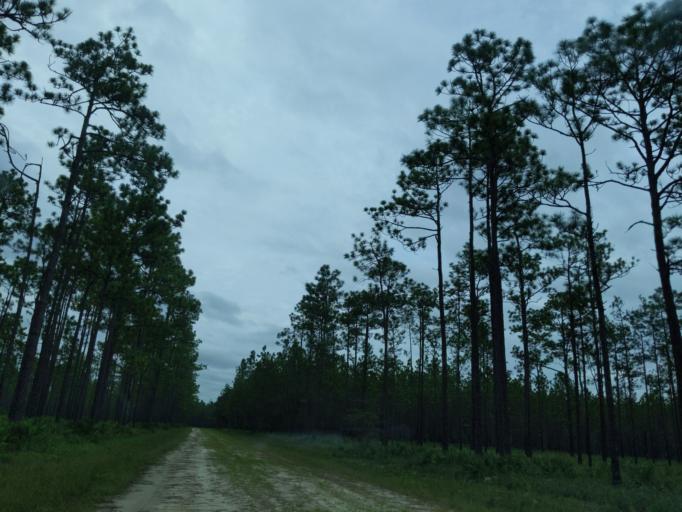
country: US
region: Florida
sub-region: Gadsden County
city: Midway
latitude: 30.3846
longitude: -84.4665
